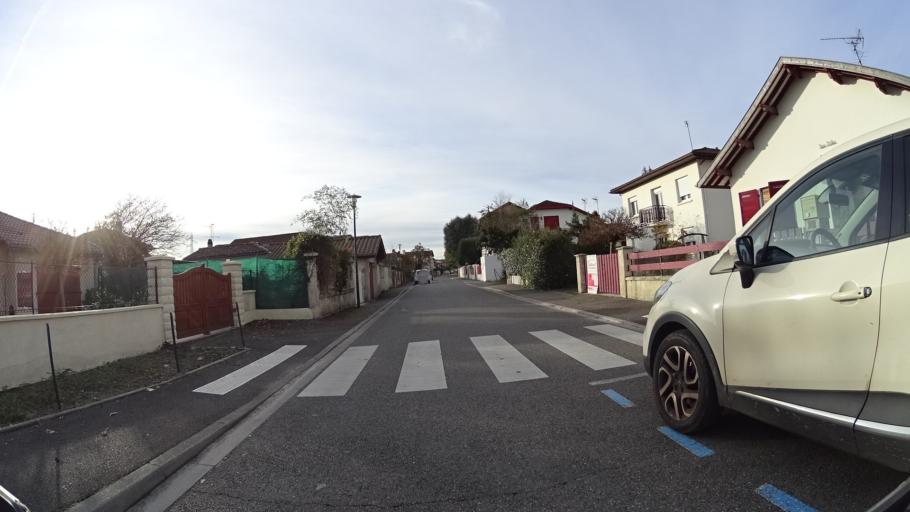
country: FR
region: Aquitaine
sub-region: Departement des Landes
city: Saint-Paul-les-Dax
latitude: 43.7224
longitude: -1.0479
